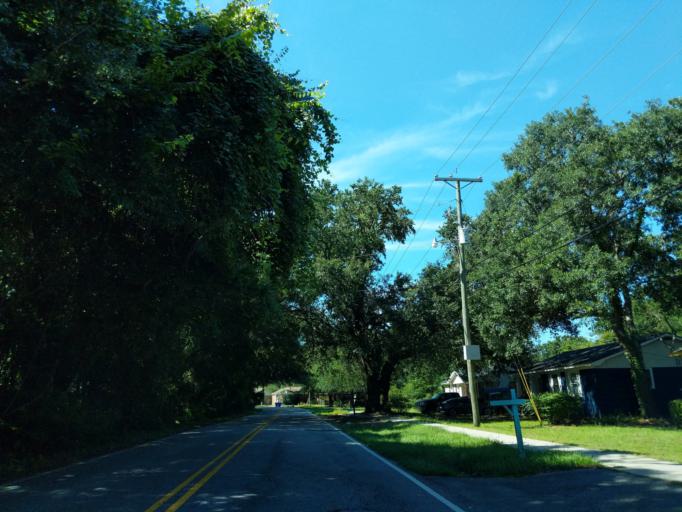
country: US
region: South Carolina
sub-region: Charleston County
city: Folly Beach
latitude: 32.7126
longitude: -79.9580
